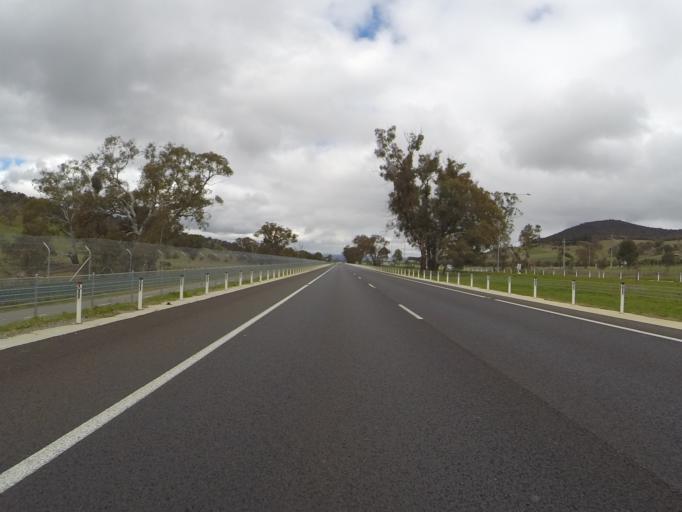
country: AU
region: Australian Capital Territory
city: Kaleen
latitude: -35.2214
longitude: 149.1961
